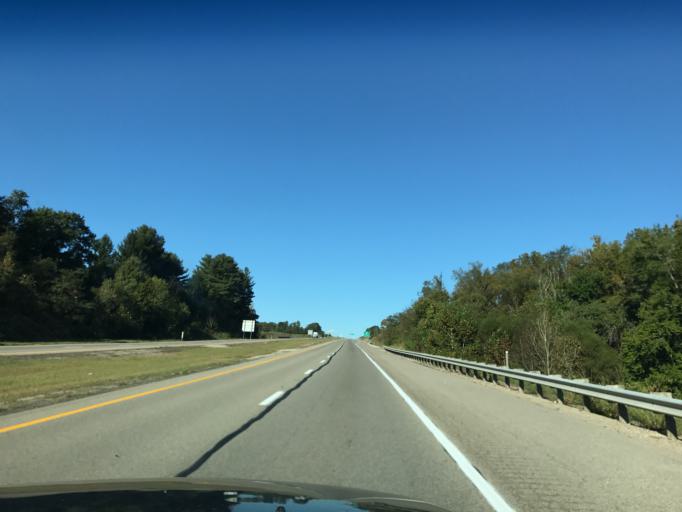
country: US
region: West Virginia
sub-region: Wood County
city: Blennerhassett
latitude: 39.2568
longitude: -81.6255
